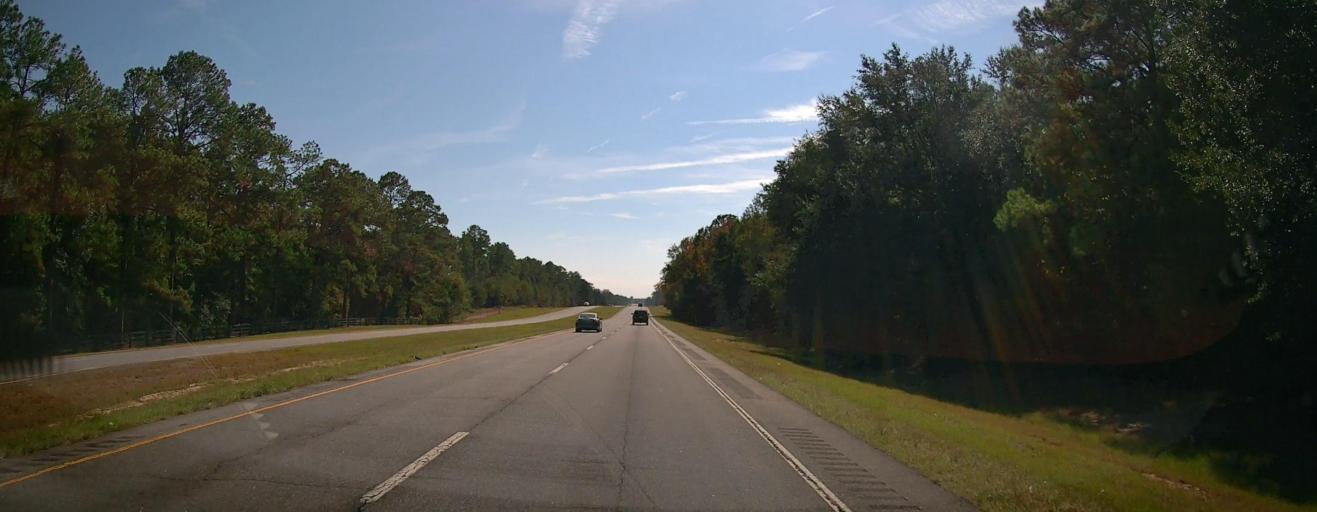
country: US
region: Georgia
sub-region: Lee County
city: Leesburg
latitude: 31.6819
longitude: -83.9945
